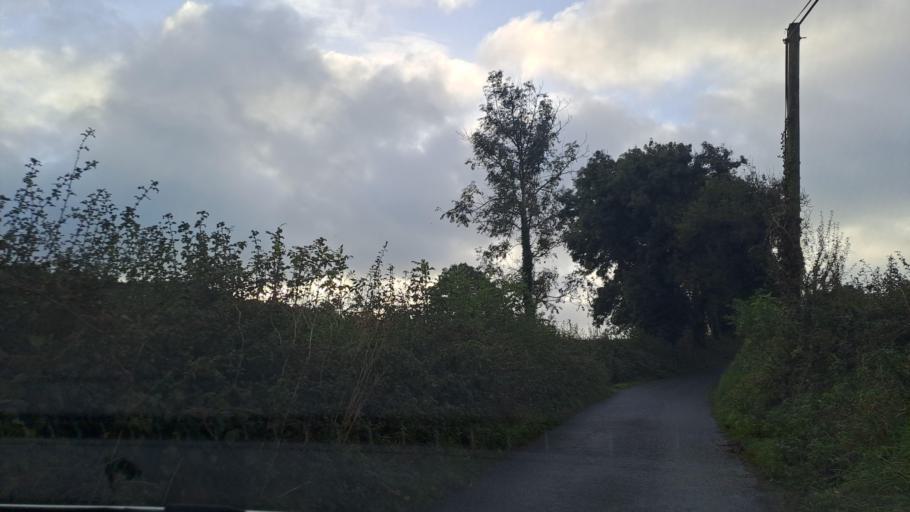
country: IE
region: Ulster
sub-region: An Cabhan
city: Kingscourt
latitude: 53.9697
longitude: -6.8433
